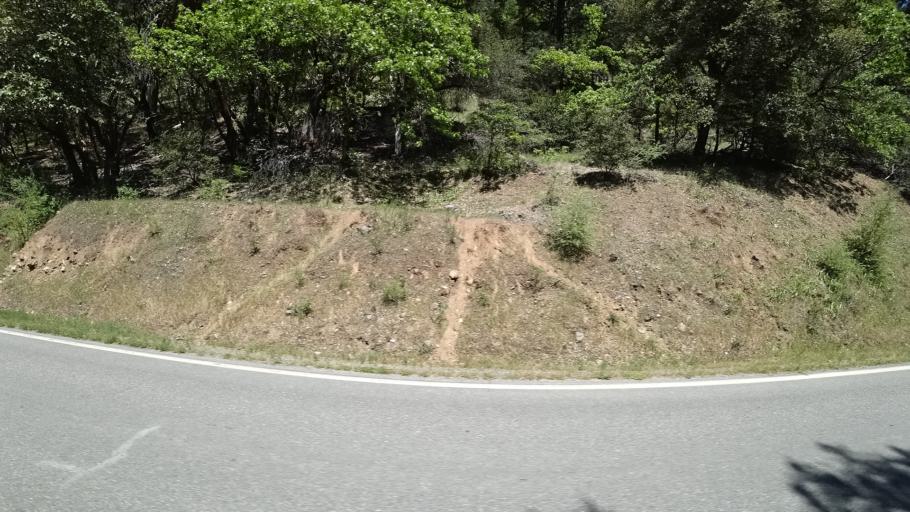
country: US
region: California
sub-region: Trinity County
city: Hayfork
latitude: 40.7521
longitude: -123.2813
